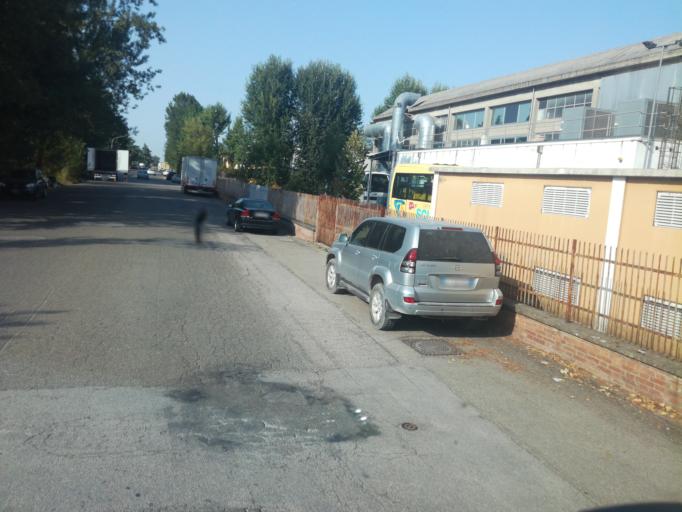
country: IT
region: Emilia-Romagna
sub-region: Provincia di Bologna
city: Progresso
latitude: 44.5516
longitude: 11.3906
